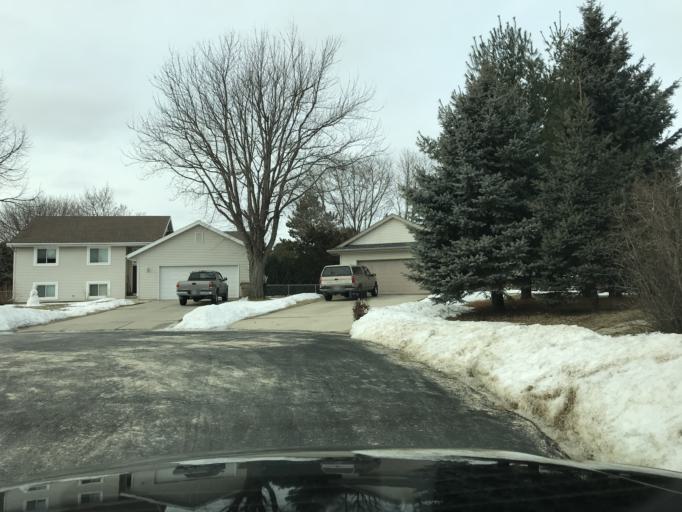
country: US
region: Wisconsin
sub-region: Dane County
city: Monona
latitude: 43.0926
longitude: -89.2696
